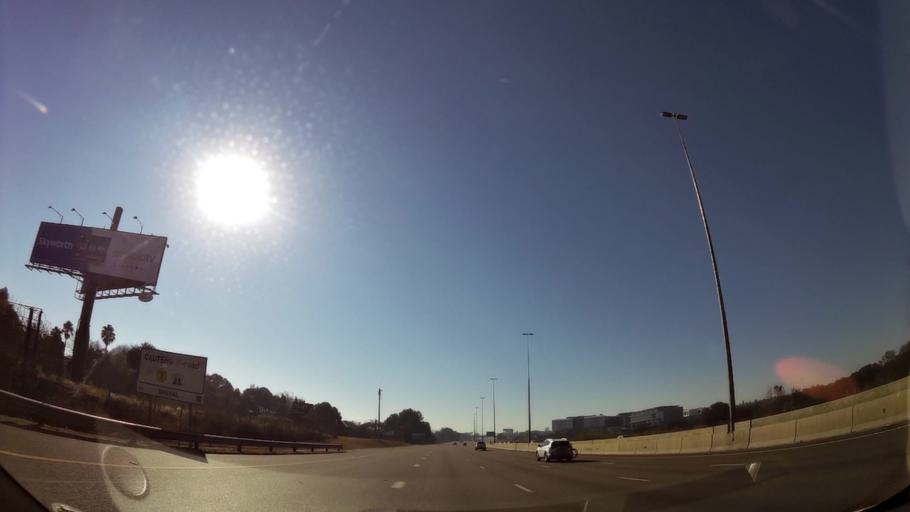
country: ZA
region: Gauteng
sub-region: City of Tshwane Metropolitan Municipality
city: Centurion
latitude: -25.8633
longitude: 28.2012
